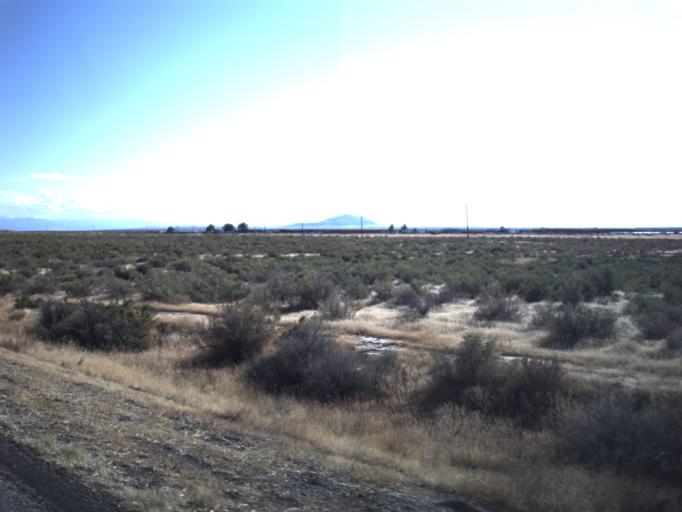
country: US
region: Utah
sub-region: Millard County
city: Delta
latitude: 39.3200
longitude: -112.4817
